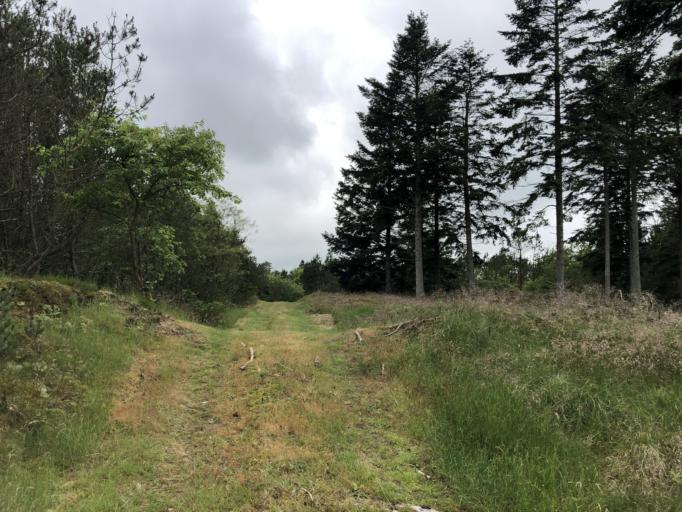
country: DK
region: Central Jutland
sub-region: Holstebro Kommune
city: Ulfborg
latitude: 56.2538
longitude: 8.3451
